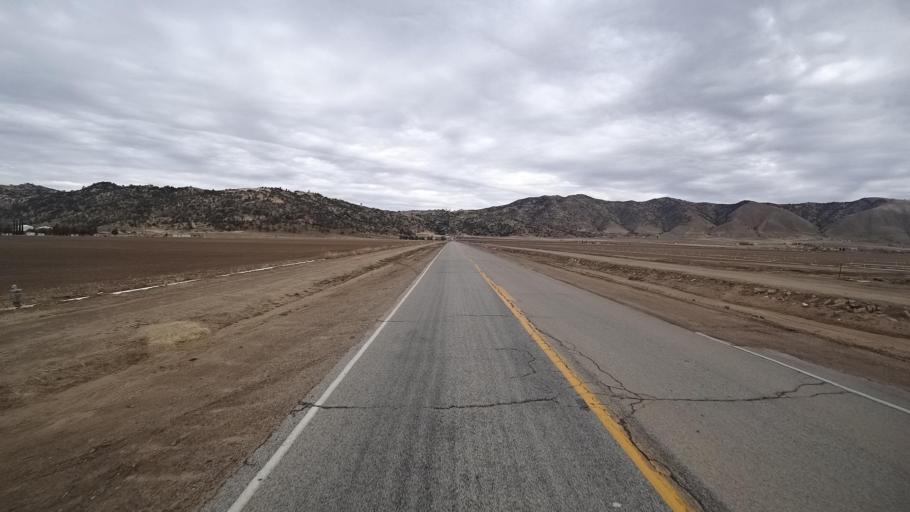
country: US
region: California
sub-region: Kern County
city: Bear Valley Springs
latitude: 35.1235
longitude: -118.5937
